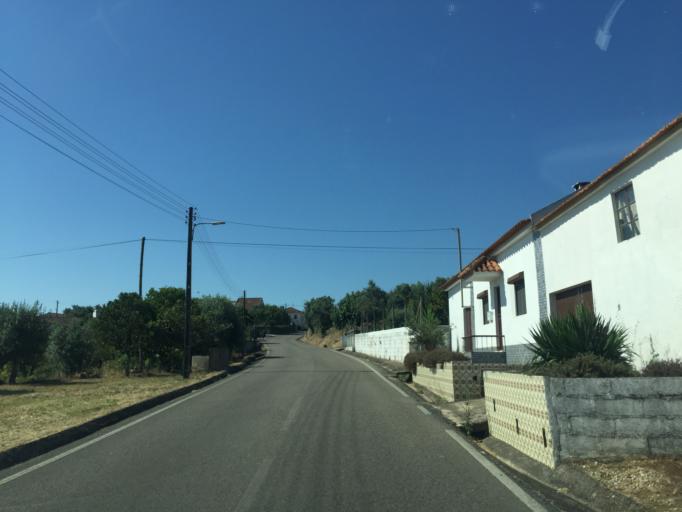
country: PT
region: Santarem
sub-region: Tomar
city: Tomar
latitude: 39.5844
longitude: -8.3275
